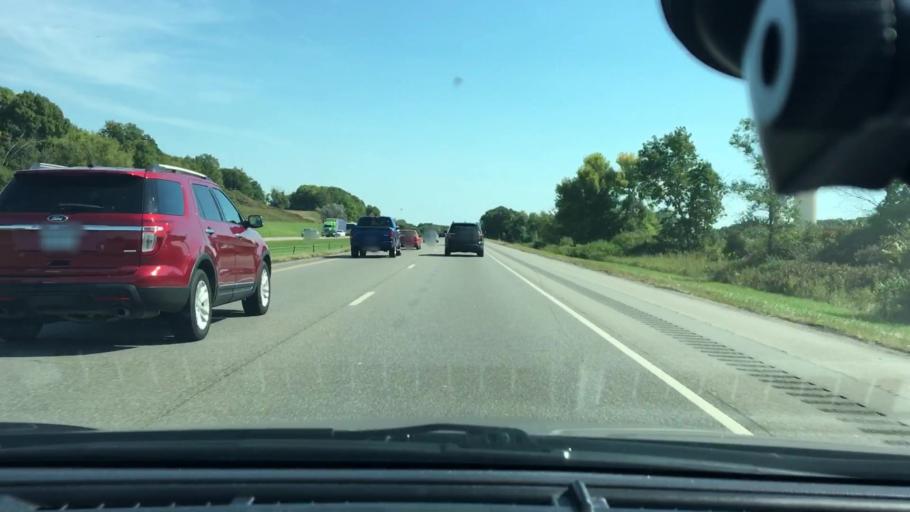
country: US
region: Minnesota
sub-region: Wright County
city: Albertville
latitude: 45.2286
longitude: -93.6230
